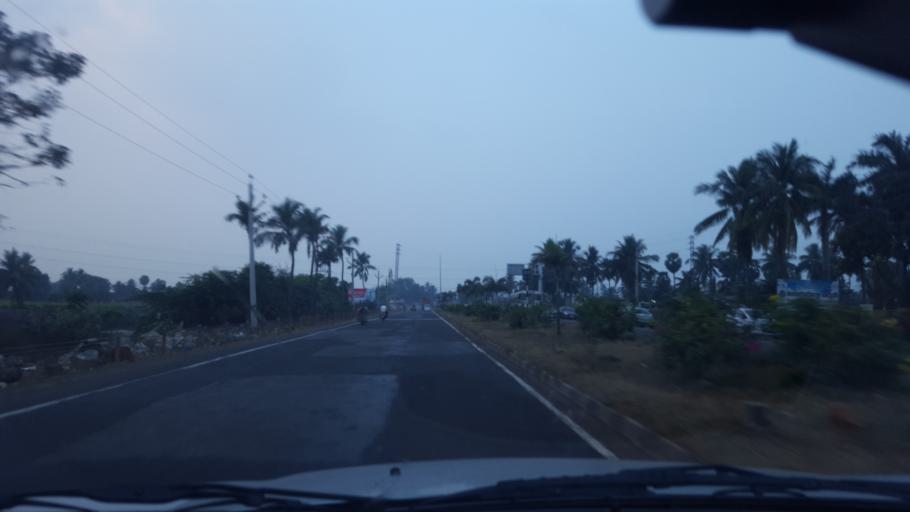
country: IN
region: Andhra Pradesh
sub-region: East Godavari
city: Rajahmundry
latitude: 16.8953
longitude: 81.7986
